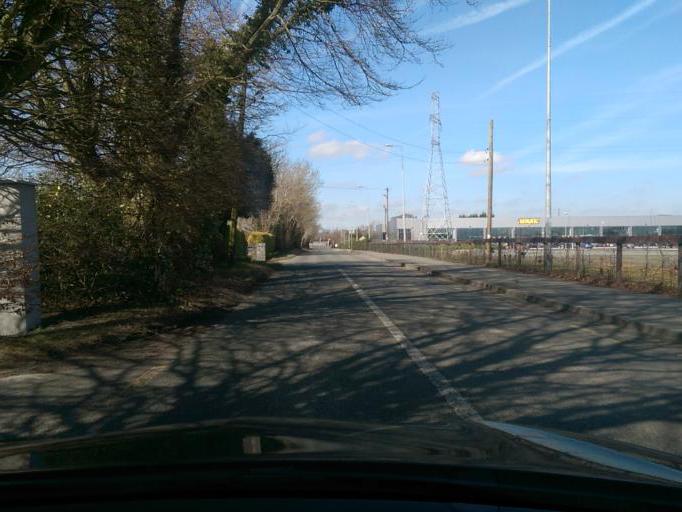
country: IE
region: Leinster
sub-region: Kildare
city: Celbridge
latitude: 53.3602
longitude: -6.5536
